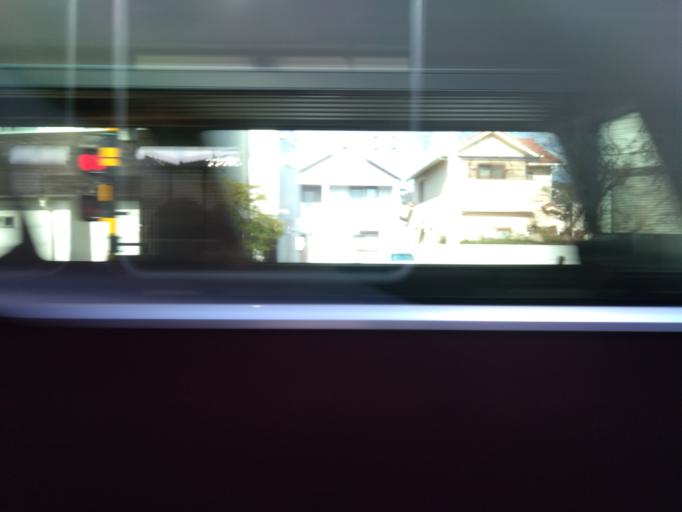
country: JP
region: Hyogo
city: Takarazuka
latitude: 34.8206
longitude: 135.3752
